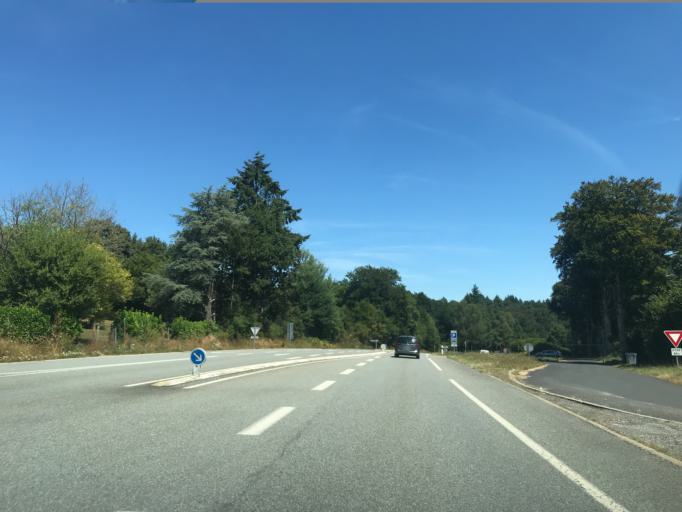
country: FR
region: Limousin
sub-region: Departement de la Correze
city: Meymac
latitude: 45.4672
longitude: 2.1436
